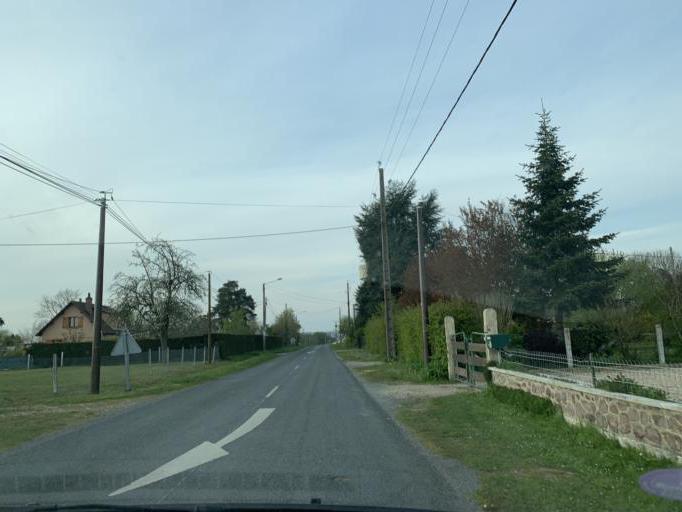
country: FR
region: Haute-Normandie
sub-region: Departement de la Seine-Maritime
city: La Mailleraye-sur-Seine
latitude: 49.4677
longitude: 0.7776
